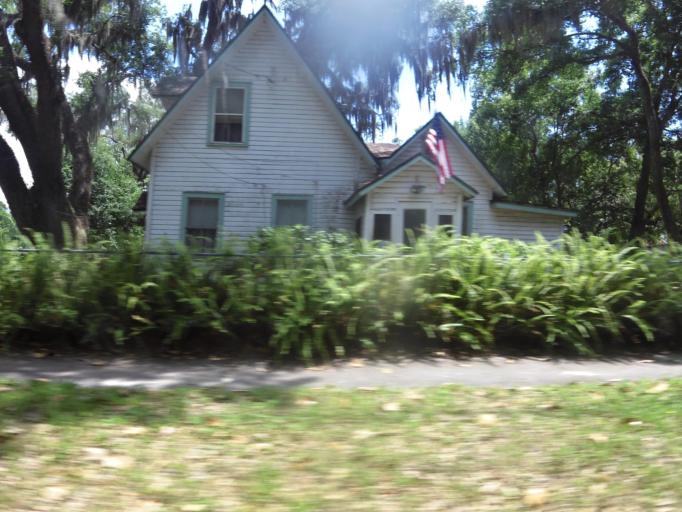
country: US
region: Florida
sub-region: Clay County
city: Orange Park
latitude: 30.1628
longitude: -81.6995
